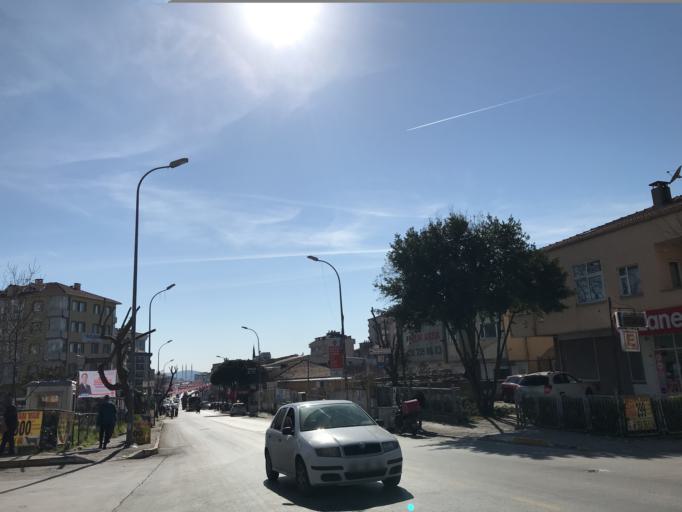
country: TR
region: Istanbul
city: Maltepe
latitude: 40.9401
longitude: 29.1426
